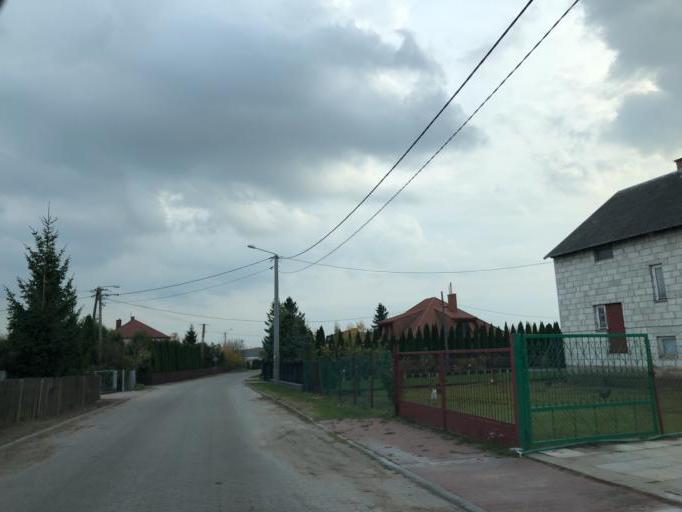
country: PL
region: Podlasie
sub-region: Lomza
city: Lomza
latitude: 53.1225
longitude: 22.0096
